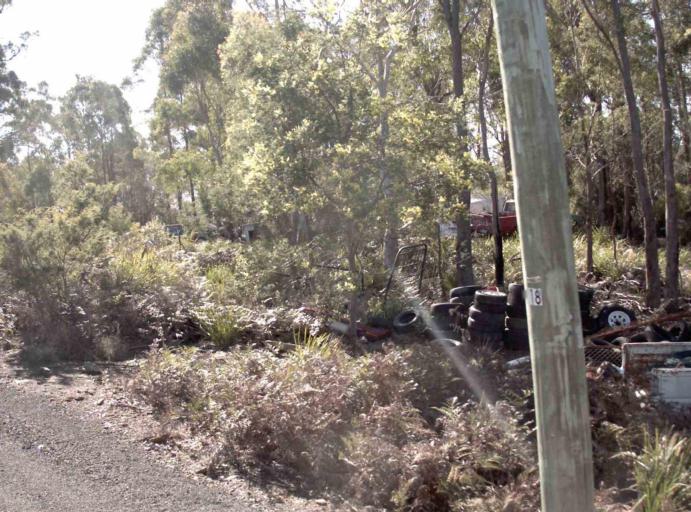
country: AU
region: Tasmania
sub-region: Launceston
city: Mayfield
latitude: -41.3181
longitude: 147.1191
